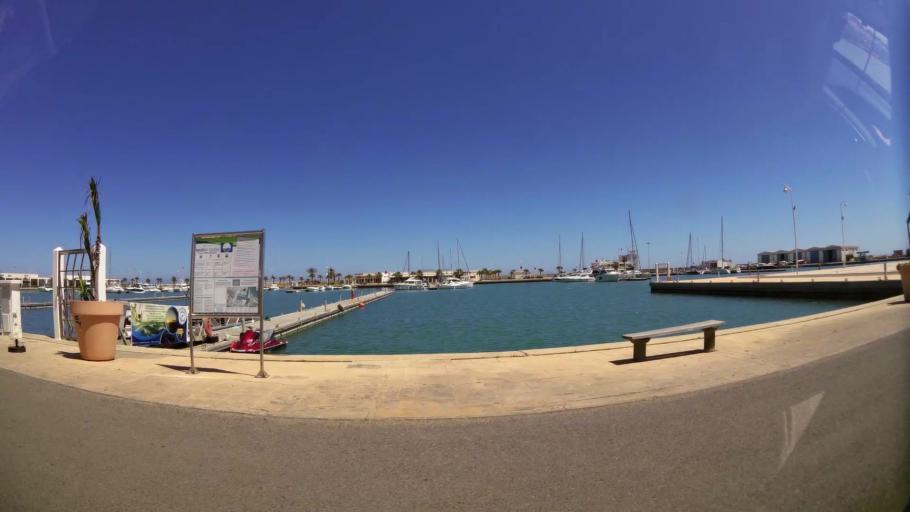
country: MA
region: Oriental
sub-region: Berkane-Taourirt
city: Madagh
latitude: 35.1089
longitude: -2.2962
